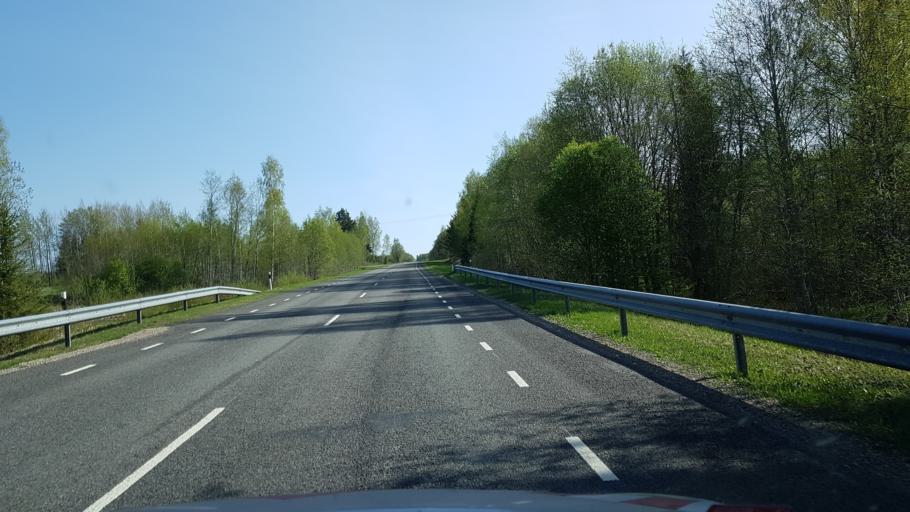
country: EE
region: Viljandimaa
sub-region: Karksi vald
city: Karksi-Nuia
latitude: 58.2111
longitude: 25.5446
